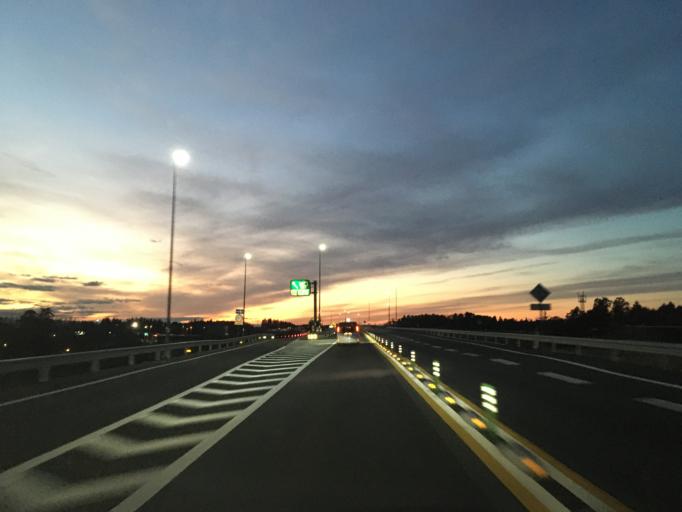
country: JP
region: Ibaraki
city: Naka
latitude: 36.0568
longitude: 140.0906
